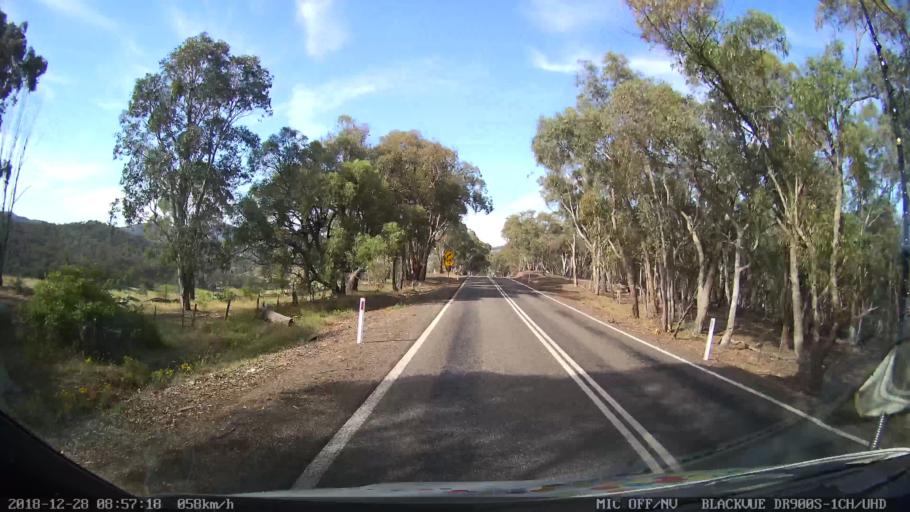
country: AU
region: New South Wales
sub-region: Upper Lachlan Shire
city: Crookwell
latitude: -34.1177
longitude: 149.3363
